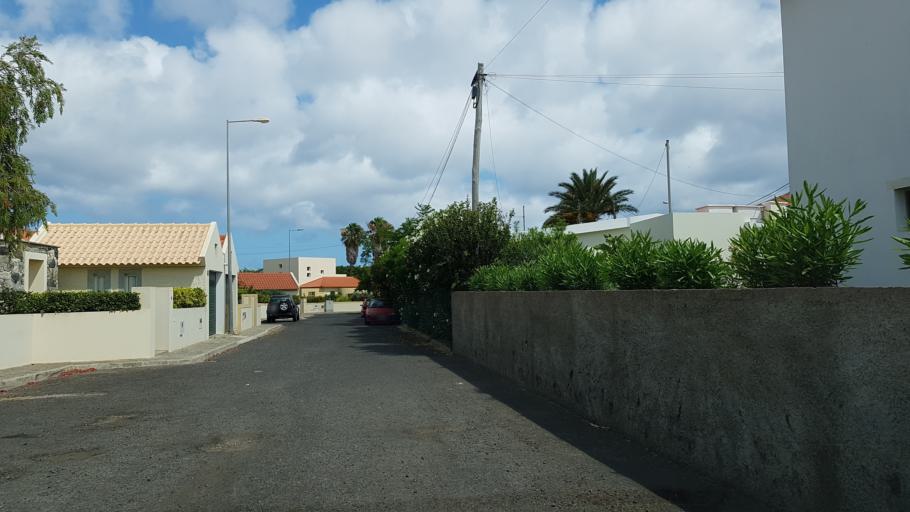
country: PT
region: Madeira
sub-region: Porto Santo
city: Vila de Porto Santo
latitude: 33.0524
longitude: -16.3501
